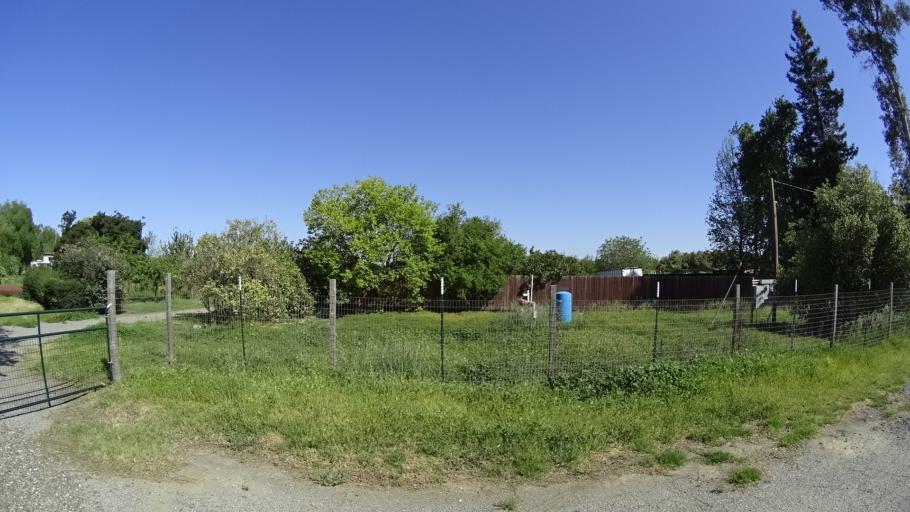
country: US
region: California
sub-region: Glenn County
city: Hamilton City
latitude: 39.7286
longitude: -122.0296
